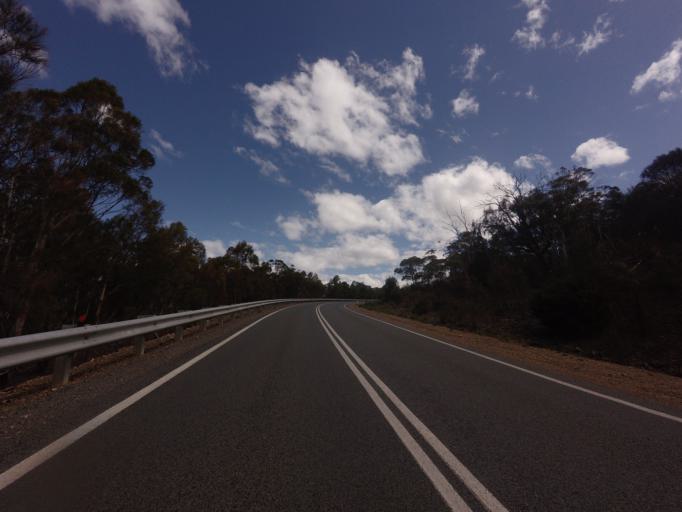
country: AU
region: Tasmania
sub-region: Break O'Day
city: St Helens
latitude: -42.0156
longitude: 147.9764
